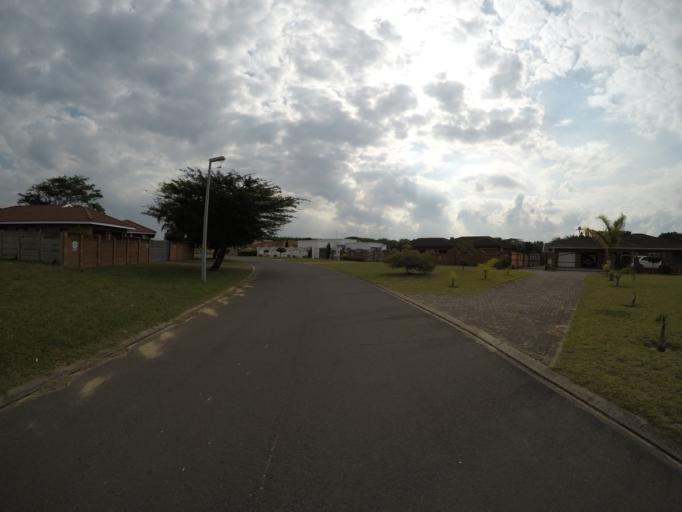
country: ZA
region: KwaZulu-Natal
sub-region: uThungulu District Municipality
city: Richards Bay
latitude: -28.7334
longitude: 32.0898
